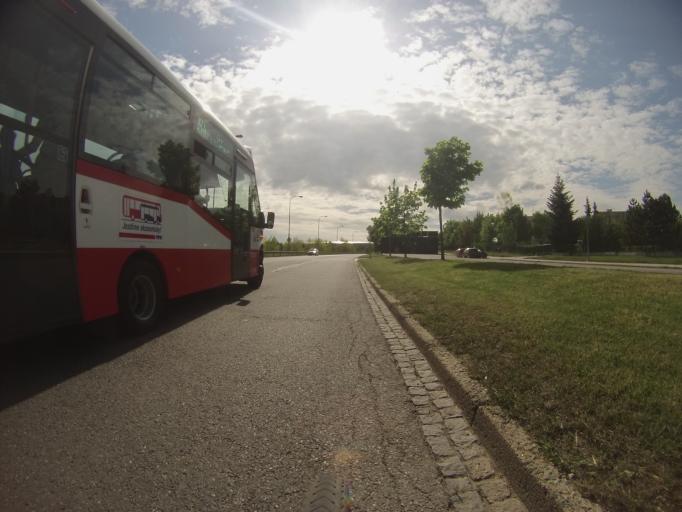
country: CZ
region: South Moravian
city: Troubsko
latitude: 49.2173
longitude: 16.5156
